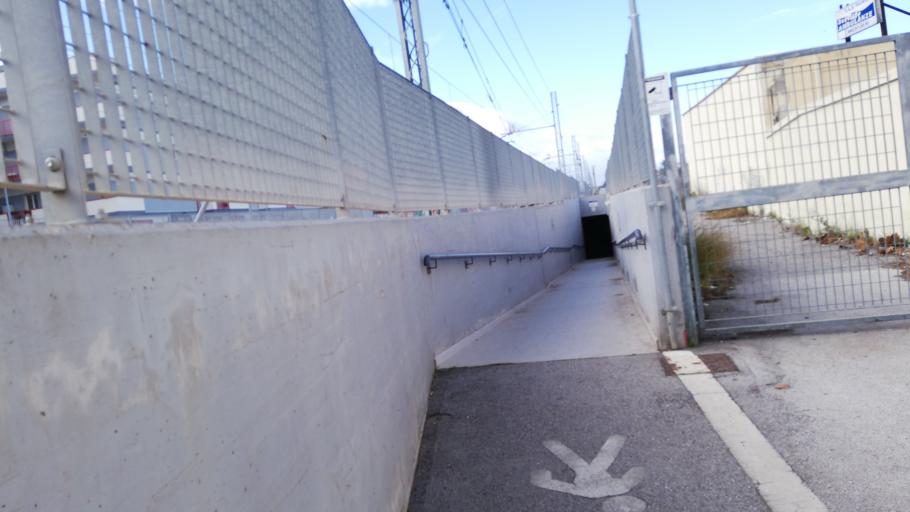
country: IT
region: Apulia
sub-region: Provincia di Bari
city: Bitonto
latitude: 41.1155
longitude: 16.6903
